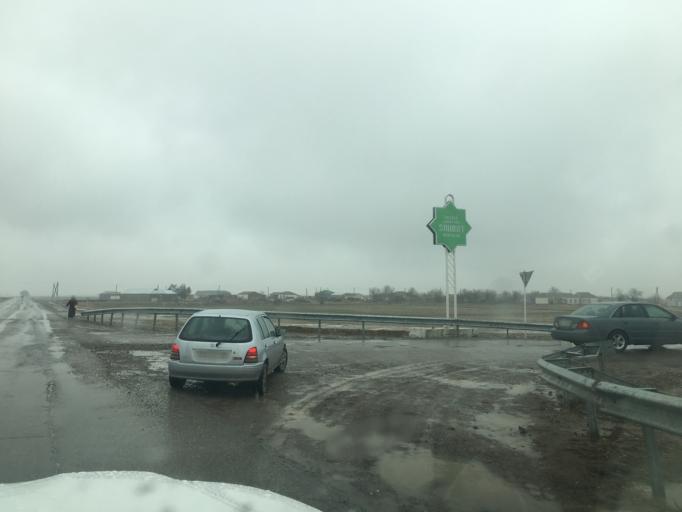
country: TM
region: Mary
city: Yoloeten
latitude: 37.3526
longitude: 62.2510
